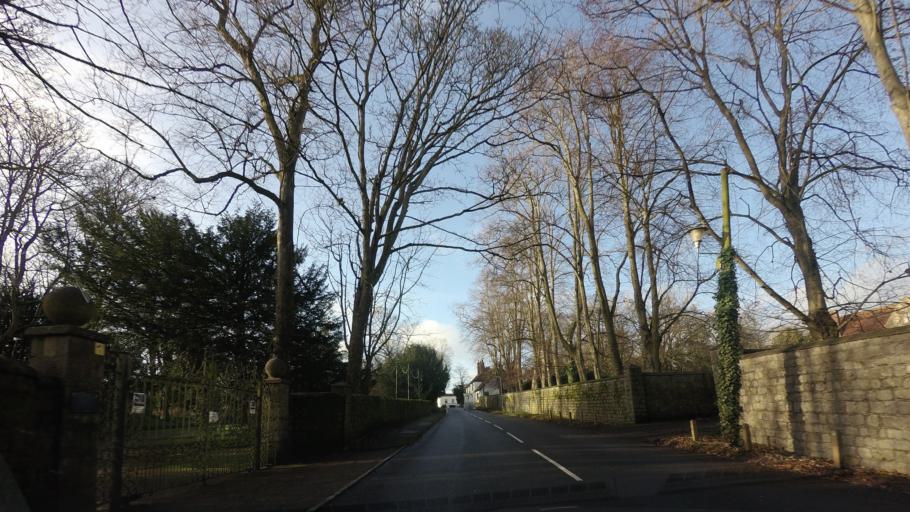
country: GB
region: England
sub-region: Kent
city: Borough Green
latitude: 51.3080
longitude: 0.3128
